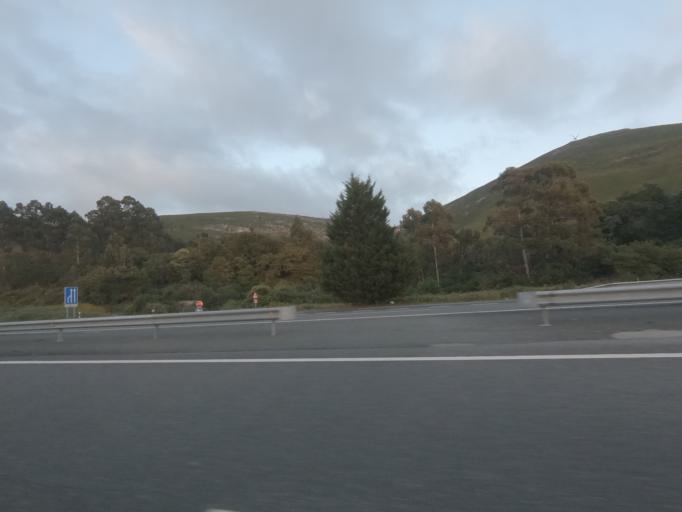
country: ES
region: Galicia
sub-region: Provincia de Pontevedra
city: Covelo
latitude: 42.1713
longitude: -8.3769
